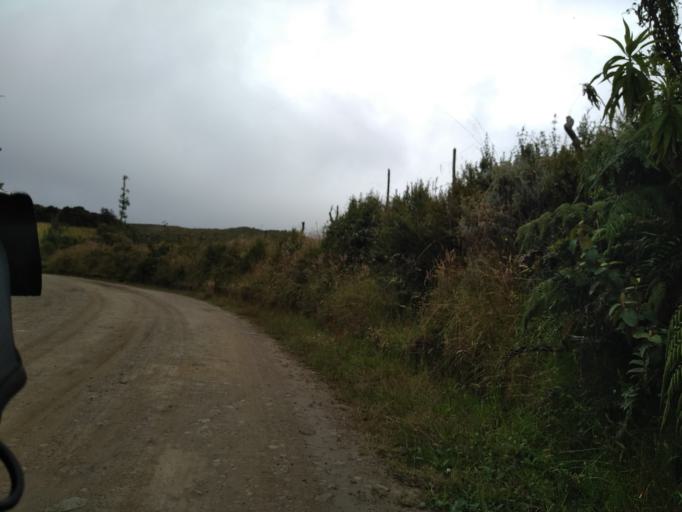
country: EC
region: Carchi
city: Tulcan
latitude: 0.7426
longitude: -77.7833
